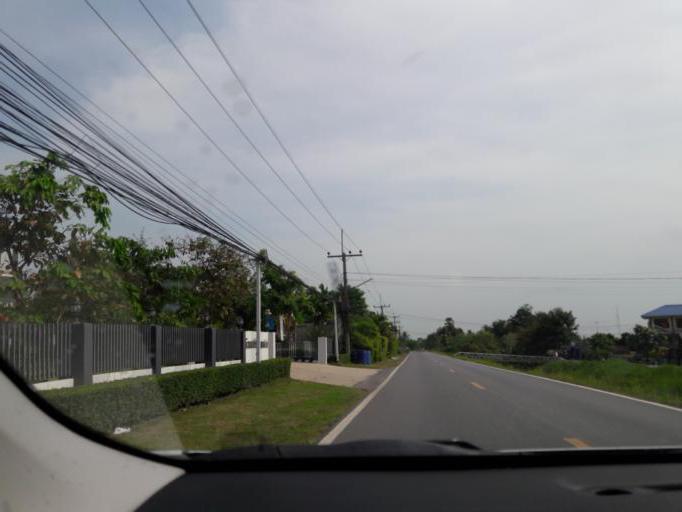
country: TH
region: Ang Thong
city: Ang Thong
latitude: 14.5868
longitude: 100.4664
